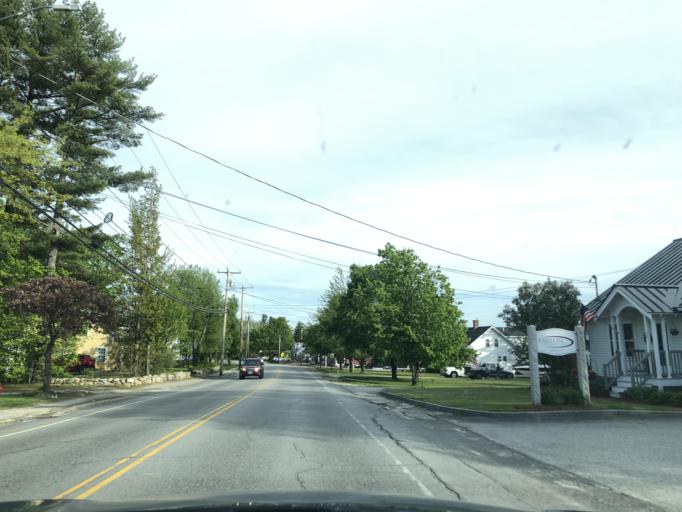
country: US
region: New Hampshire
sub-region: Merrimack County
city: New London
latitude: 43.4199
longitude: -71.9916
